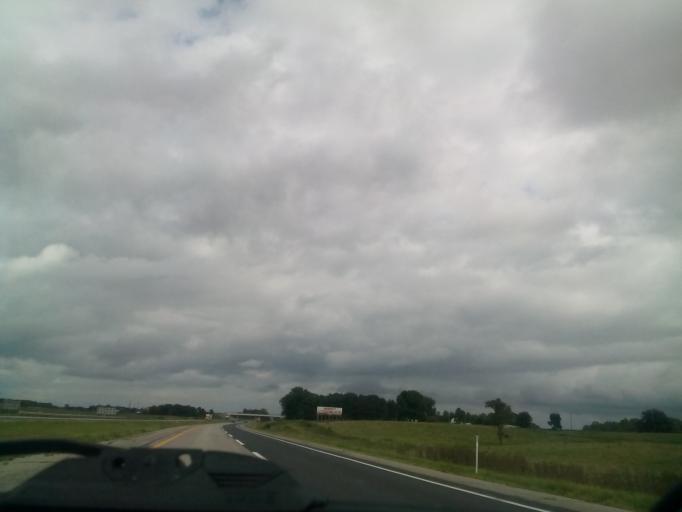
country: US
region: Indiana
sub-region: Steuben County
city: Fremont
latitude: 41.7042
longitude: -84.9252
